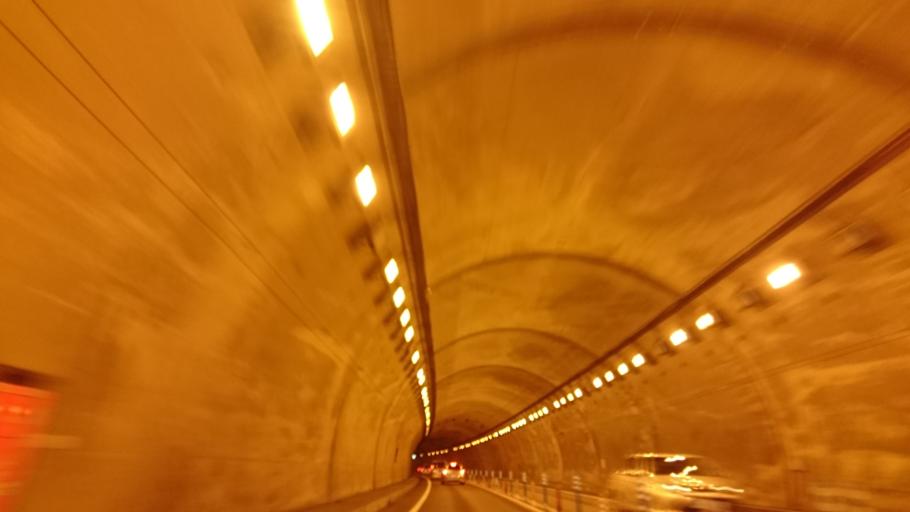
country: JP
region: Gifu
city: Gujo
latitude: 35.9758
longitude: 136.8976
